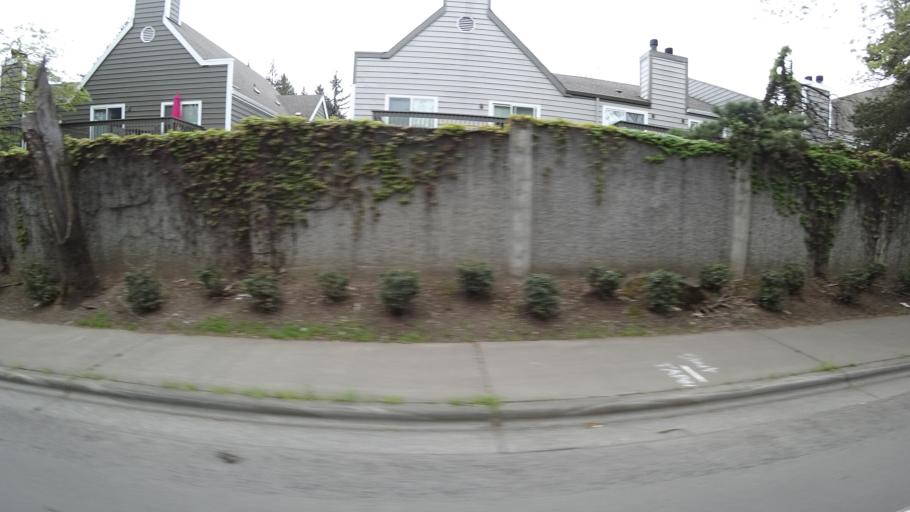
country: US
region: Oregon
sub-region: Washington County
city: Beaverton
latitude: 45.4614
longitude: -122.8260
